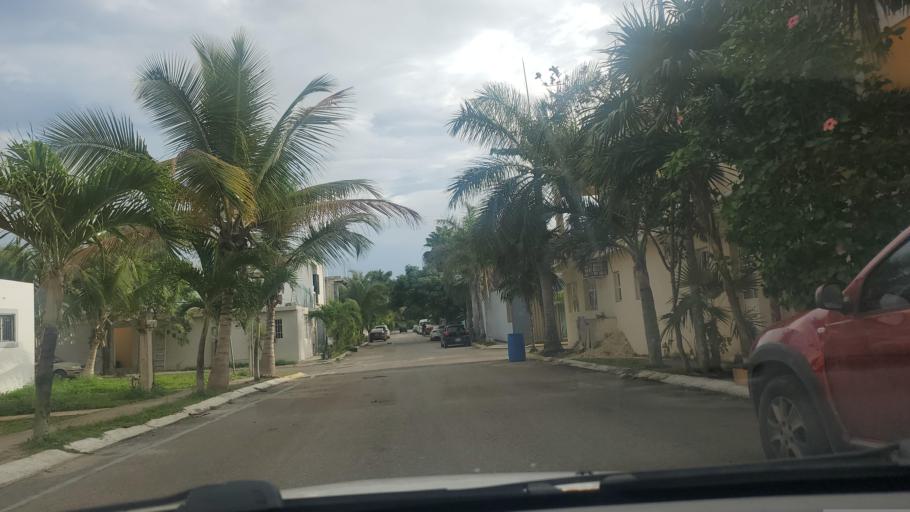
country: MX
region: Quintana Roo
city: Tulum
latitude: 20.2156
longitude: -87.4559
